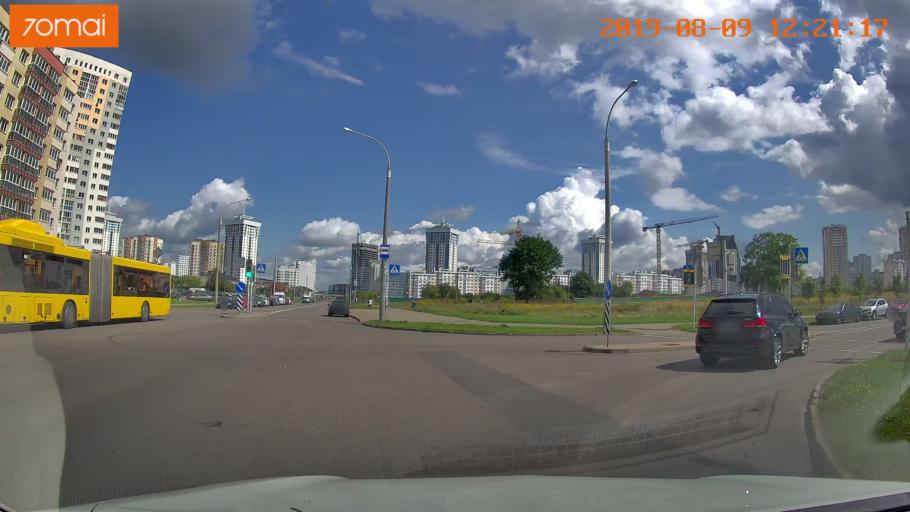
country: BY
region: Minsk
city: Zhdanovichy
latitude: 53.9345
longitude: 27.4615
